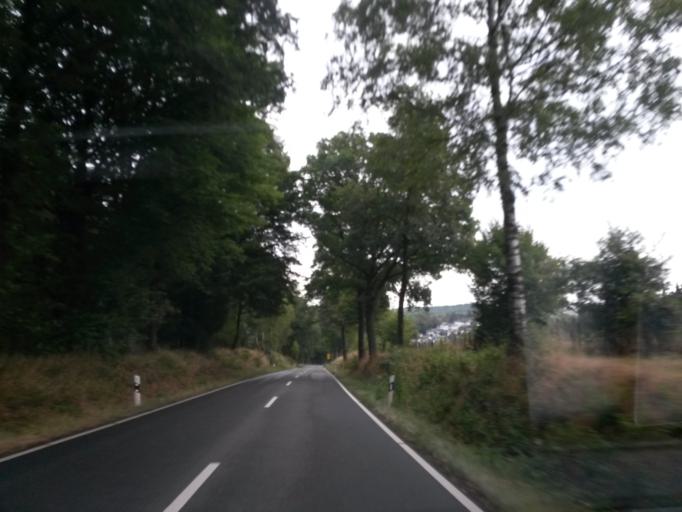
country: DE
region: North Rhine-Westphalia
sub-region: Regierungsbezirk Koln
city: Numbrecht
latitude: 50.8939
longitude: 7.5359
